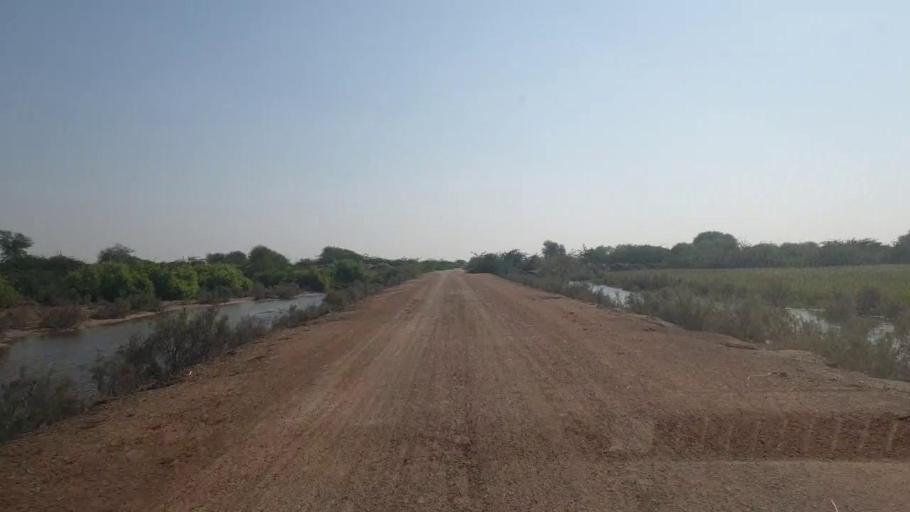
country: PK
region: Sindh
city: Badin
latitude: 24.5635
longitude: 68.8455
